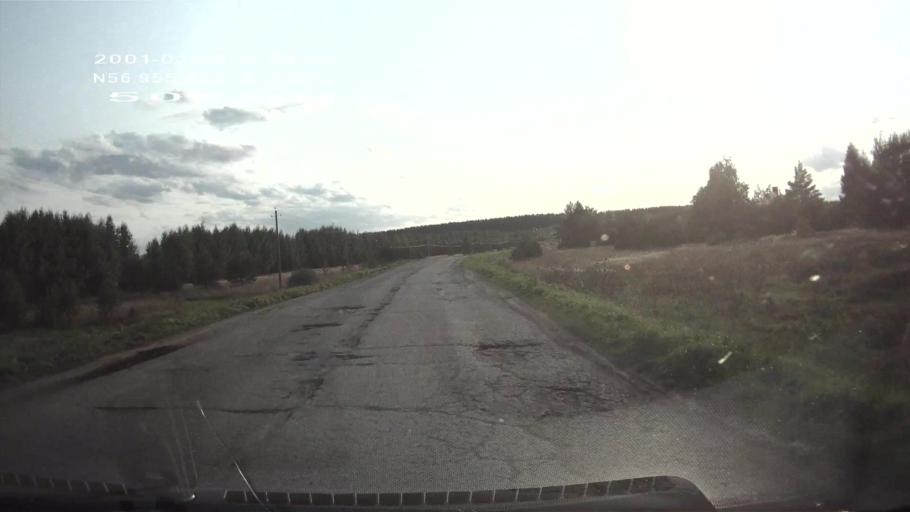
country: RU
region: Mariy-El
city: Kuzhener
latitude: 56.9547
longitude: 48.7635
